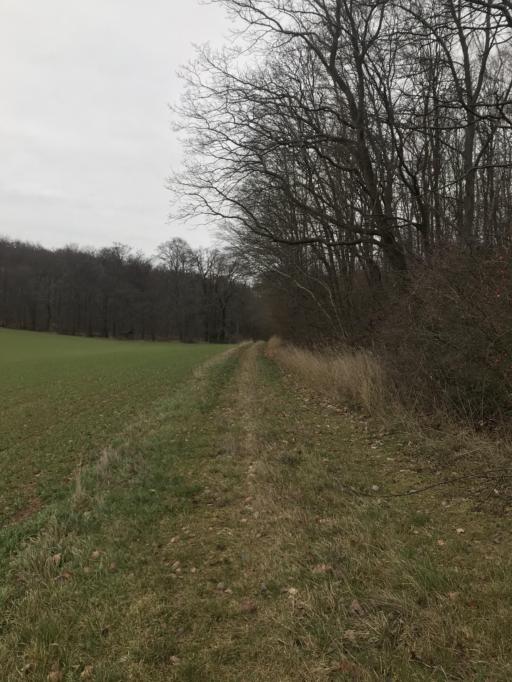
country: DE
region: Saxony-Anhalt
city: Wippra
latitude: 51.6296
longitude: 11.3214
